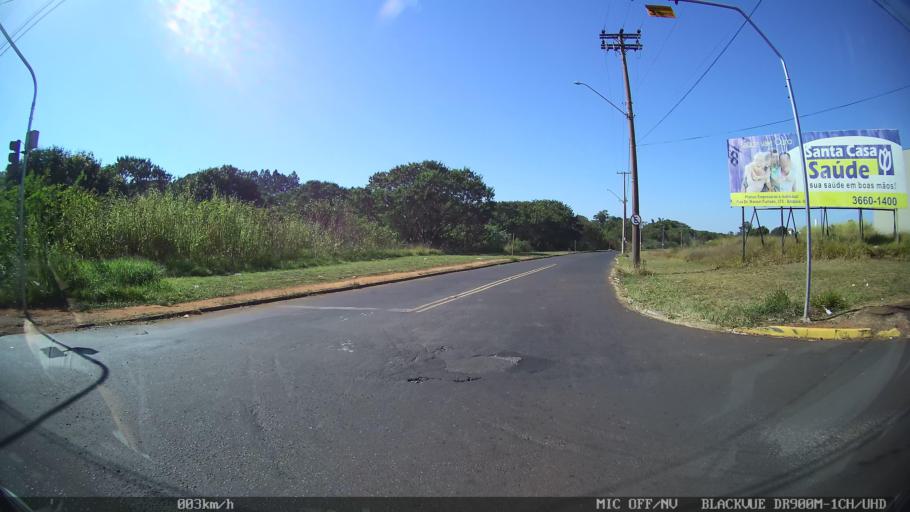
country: BR
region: Sao Paulo
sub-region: Batatais
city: Batatais
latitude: -20.8863
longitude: -47.5826
